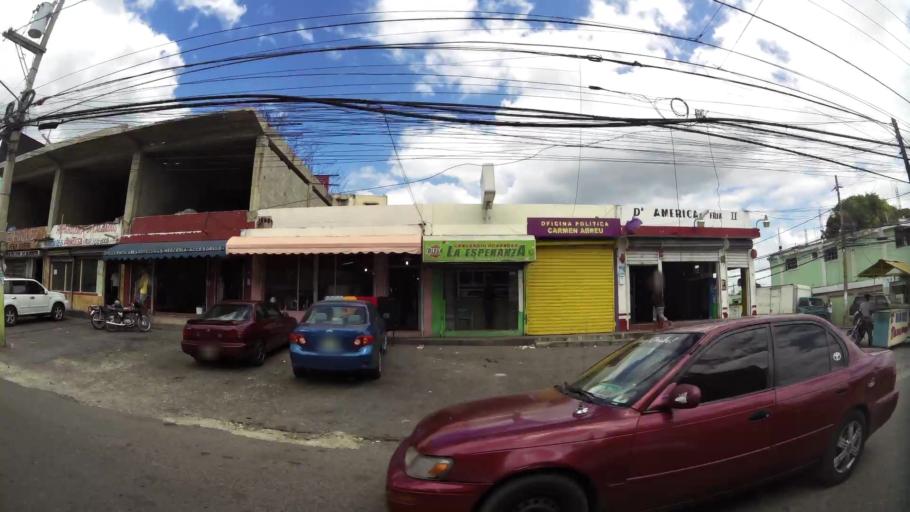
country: DO
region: Nacional
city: Ensanche Luperon
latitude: 18.5304
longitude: -69.9063
